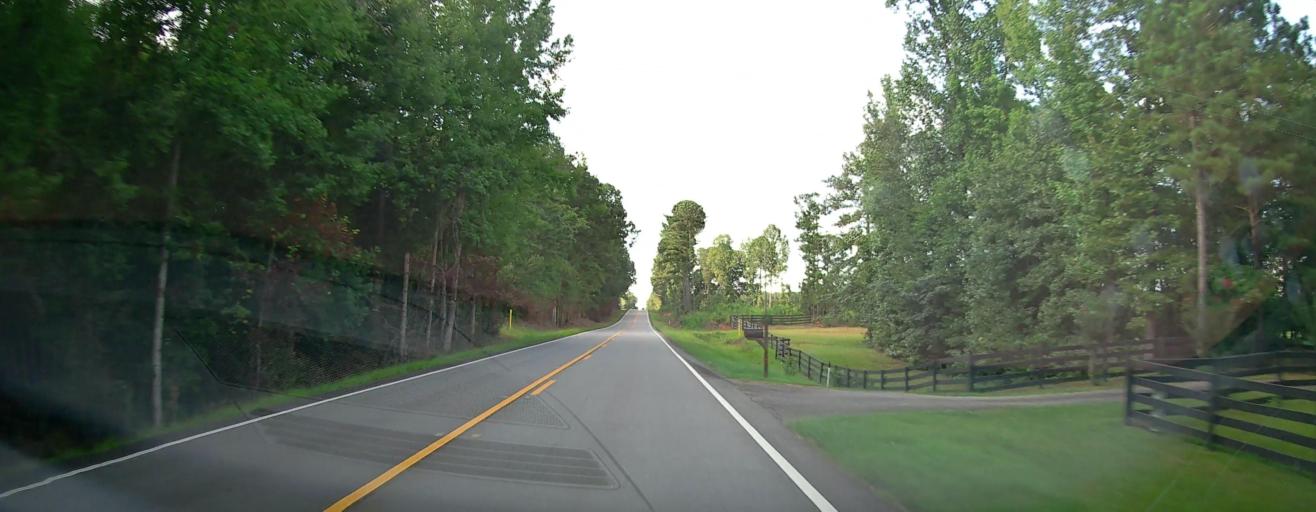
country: US
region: Georgia
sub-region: Monroe County
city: Forsyth
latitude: 32.8892
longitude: -83.9948
